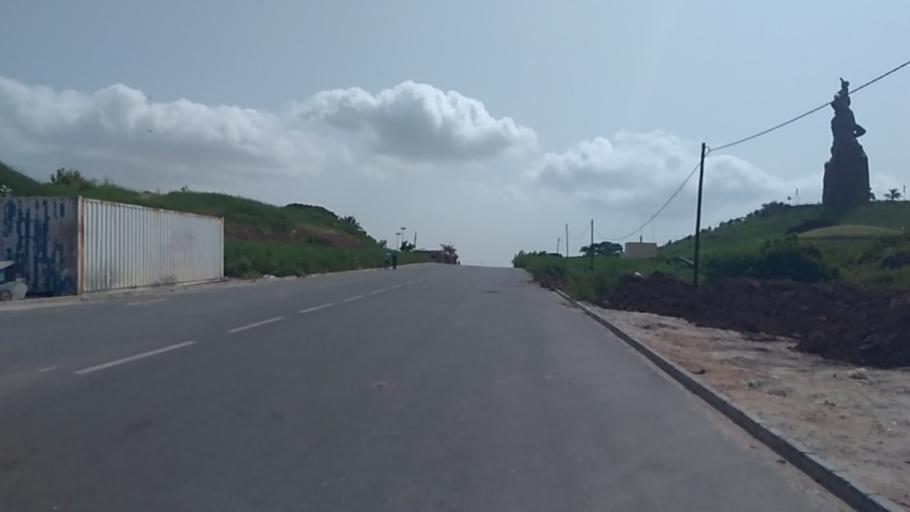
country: SN
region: Dakar
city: Mermoz Boabab
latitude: 14.7227
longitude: -17.4982
